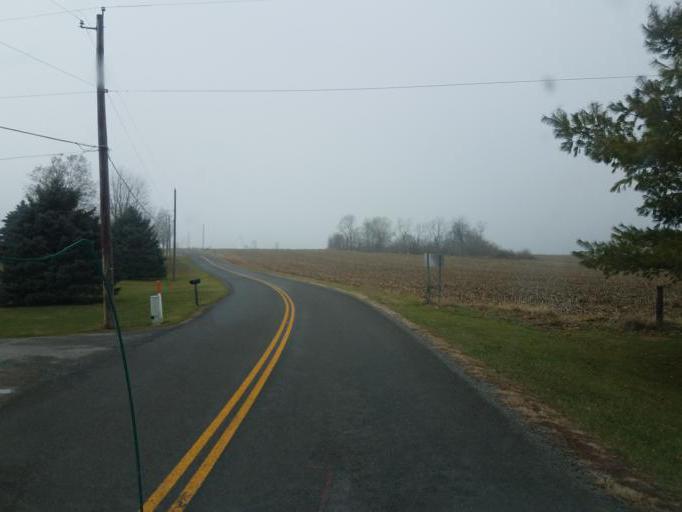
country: US
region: Ohio
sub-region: Champaign County
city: North Lewisburg
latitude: 40.2947
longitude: -83.5845
